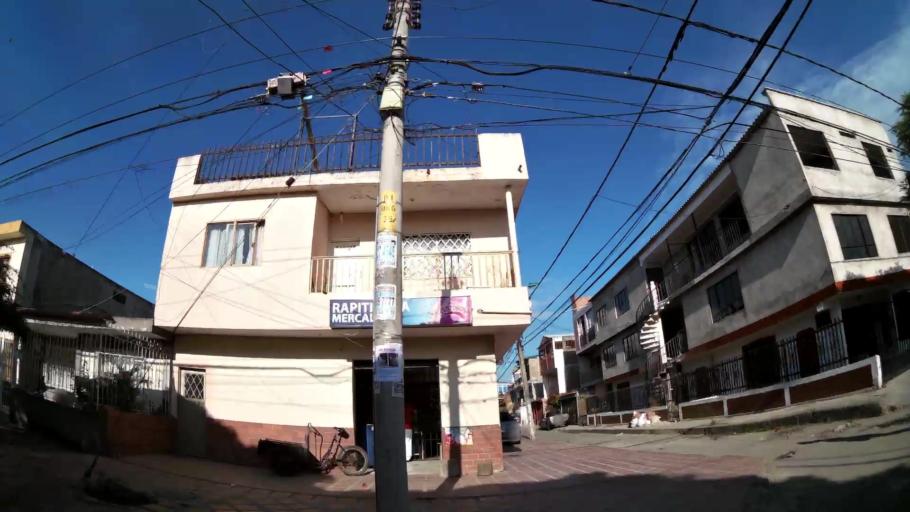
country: CO
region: Valle del Cauca
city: Cali
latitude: 3.4255
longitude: -76.5143
